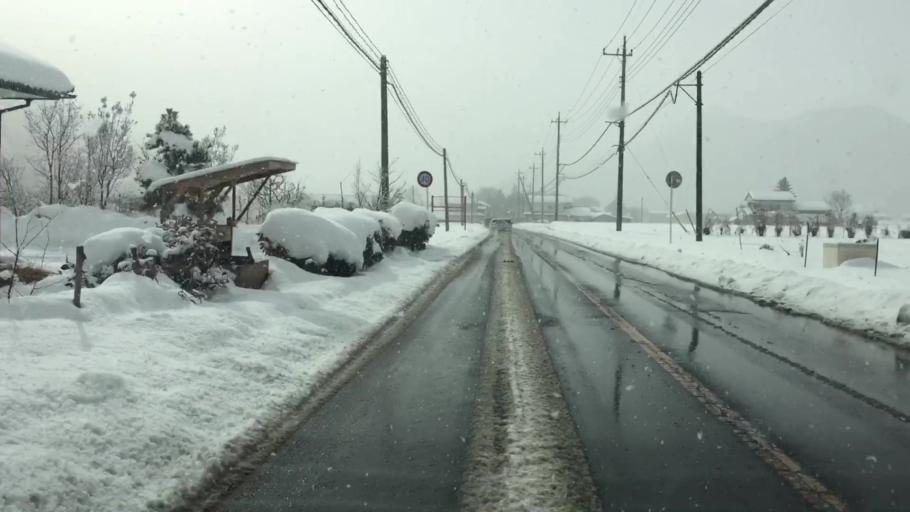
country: JP
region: Gunma
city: Numata
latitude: 36.7035
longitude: 139.0656
